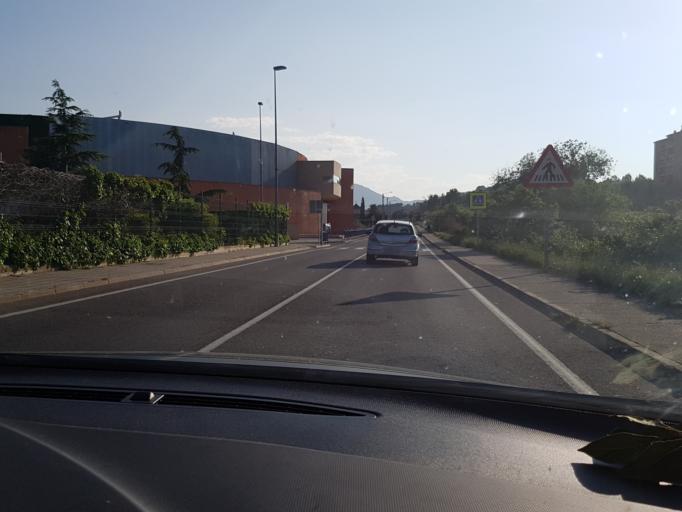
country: ES
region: La Rioja
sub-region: Provincia de La Rioja
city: Arnedo
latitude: 42.2224
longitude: -2.1062
